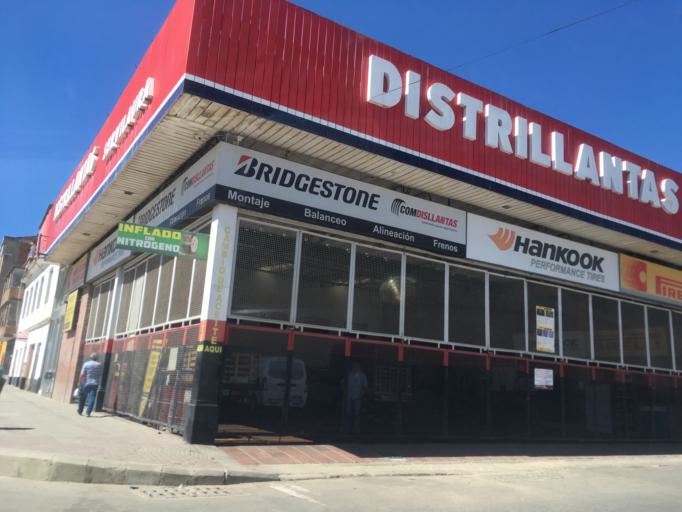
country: CO
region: Boyaca
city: Duitama
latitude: 5.8246
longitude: -73.0315
